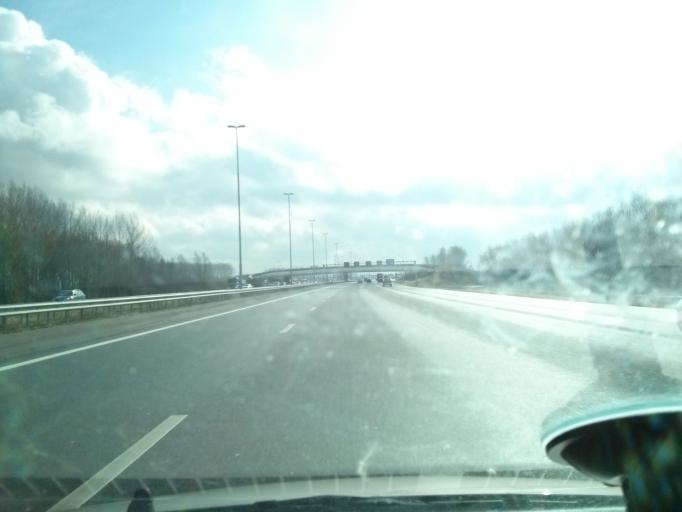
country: NL
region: Gelderland
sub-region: Gemeente Culemborg
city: Culemborg
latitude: 51.9199
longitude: 5.1735
